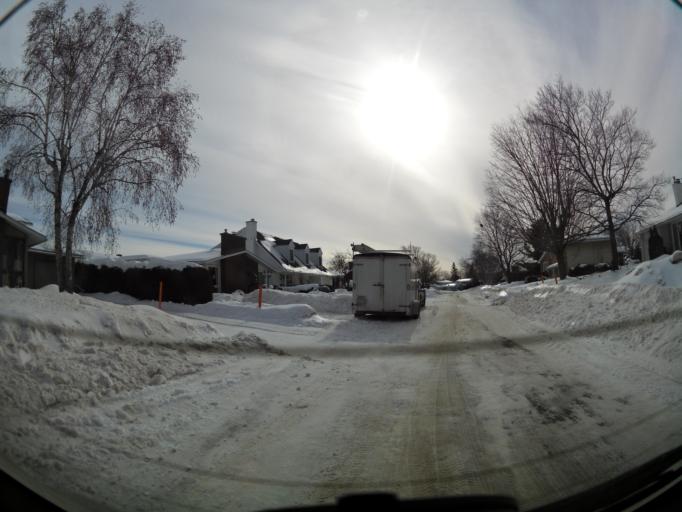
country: CA
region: Ontario
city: Ottawa
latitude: 45.4426
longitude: -75.5994
